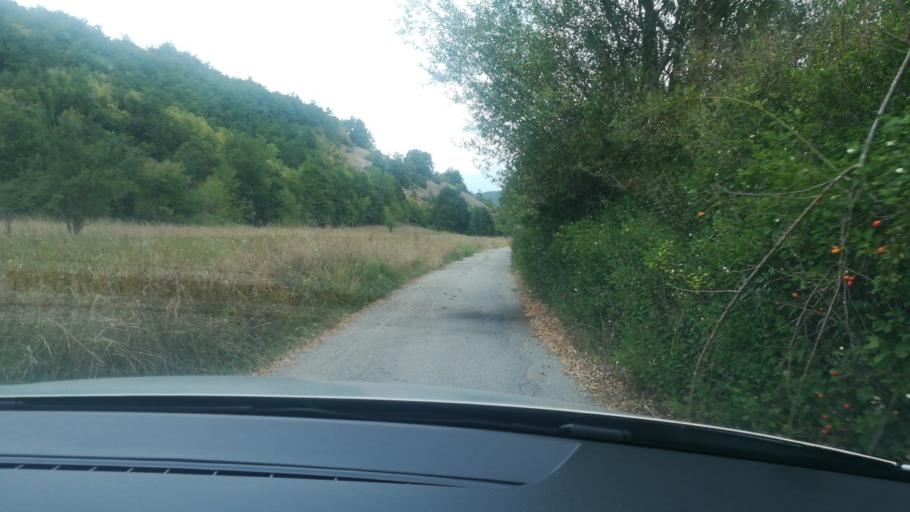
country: MK
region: Debarca
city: Belcista
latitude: 41.2871
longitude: 20.8305
